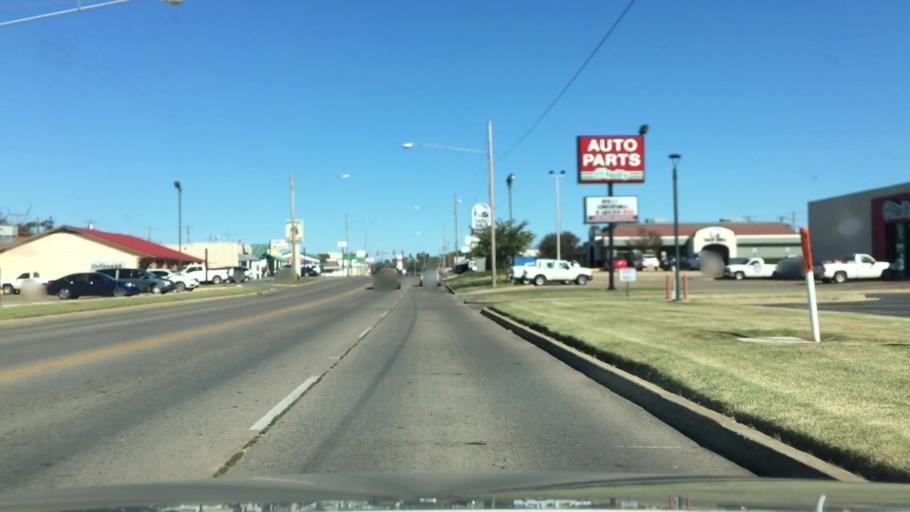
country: US
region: Oklahoma
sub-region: Cherokee County
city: Tahlequah
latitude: 35.8985
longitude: -94.9757
